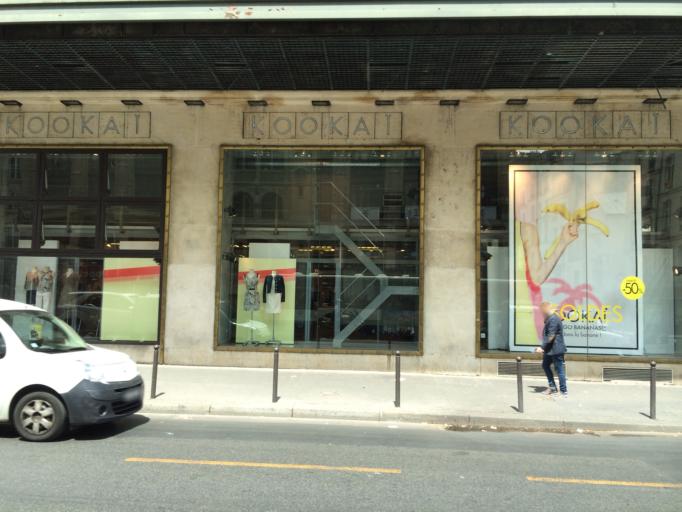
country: FR
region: Ile-de-France
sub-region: Paris
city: Paris
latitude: 48.8667
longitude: 2.3510
